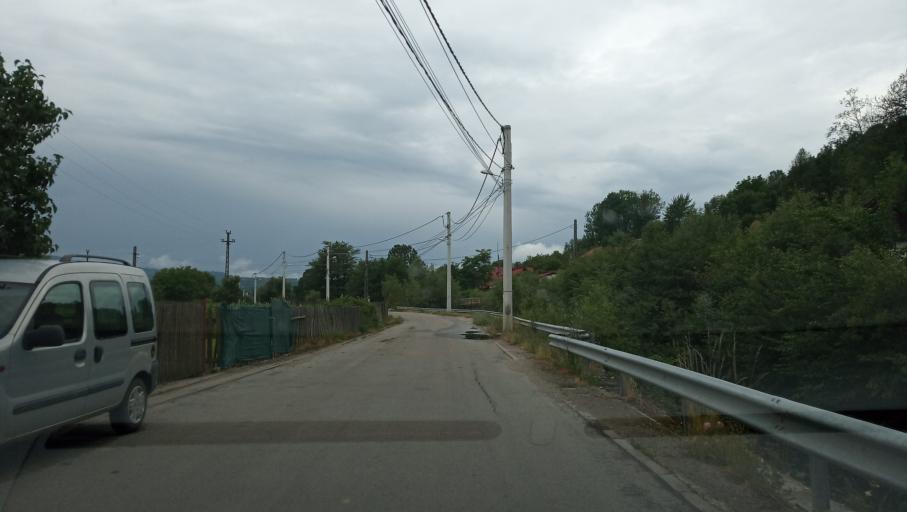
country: RO
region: Hunedoara
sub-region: Oras Petrila
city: Petrila
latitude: 45.4612
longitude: 23.4198
